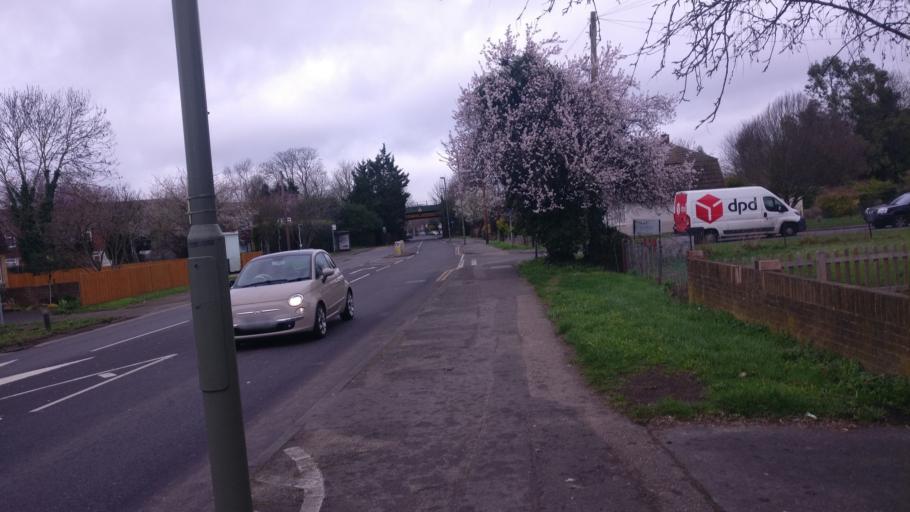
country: GB
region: England
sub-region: Surrey
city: Staines
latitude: 51.4291
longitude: -0.5135
